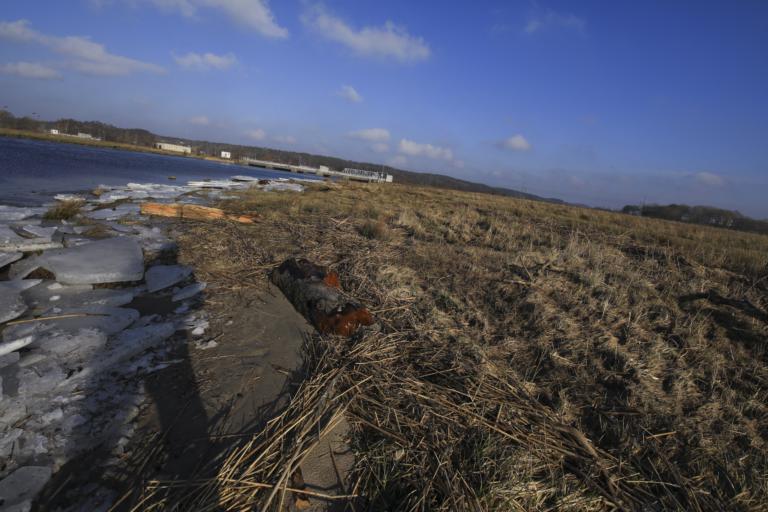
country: SE
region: Halland
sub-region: Kungsbacka Kommun
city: Frillesas
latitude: 57.2246
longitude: 12.2110
